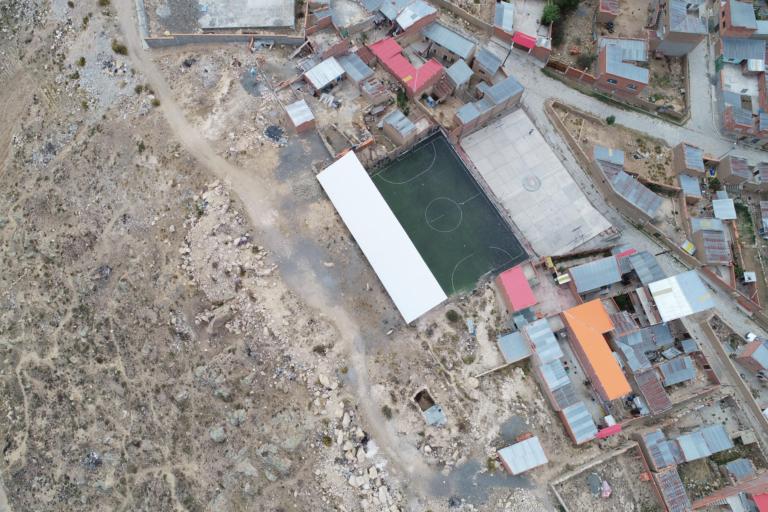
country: BO
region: La Paz
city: Achacachi
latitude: -16.0422
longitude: -68.6814
